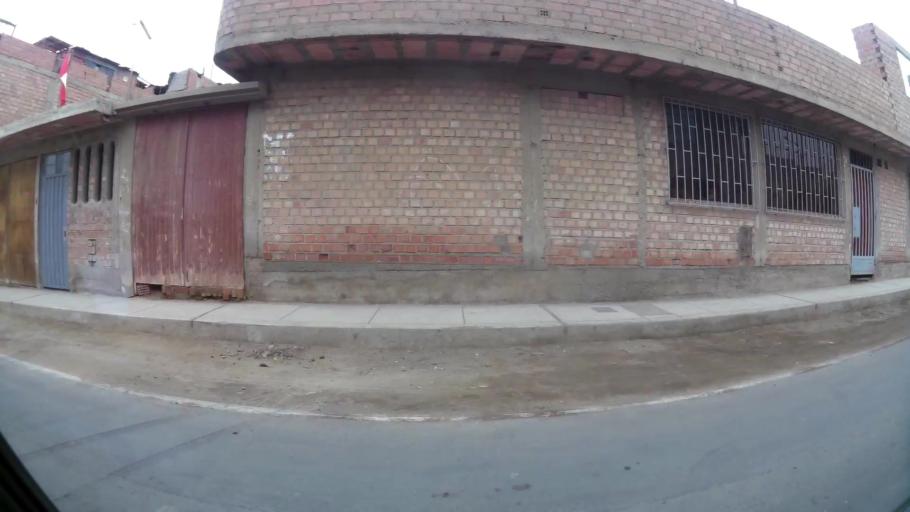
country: PE
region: Lima
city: Ventanilla
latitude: -11.9346
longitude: -77.0855
